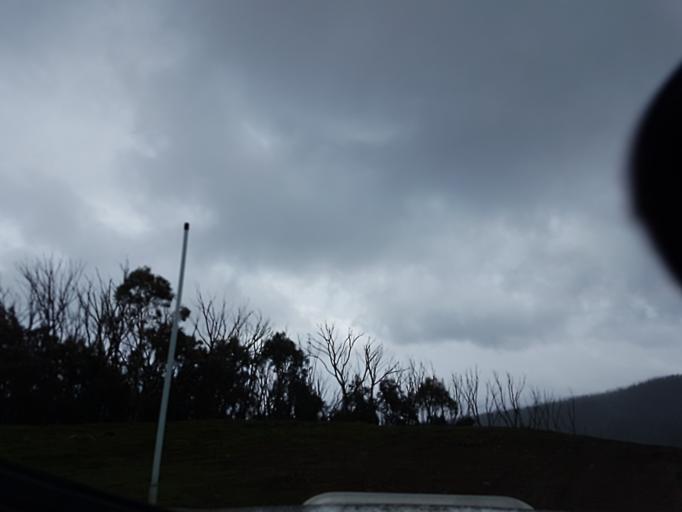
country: AU
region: Victoria
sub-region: Alpine
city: Mount Beauty
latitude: -37.0885
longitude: 147.1035
